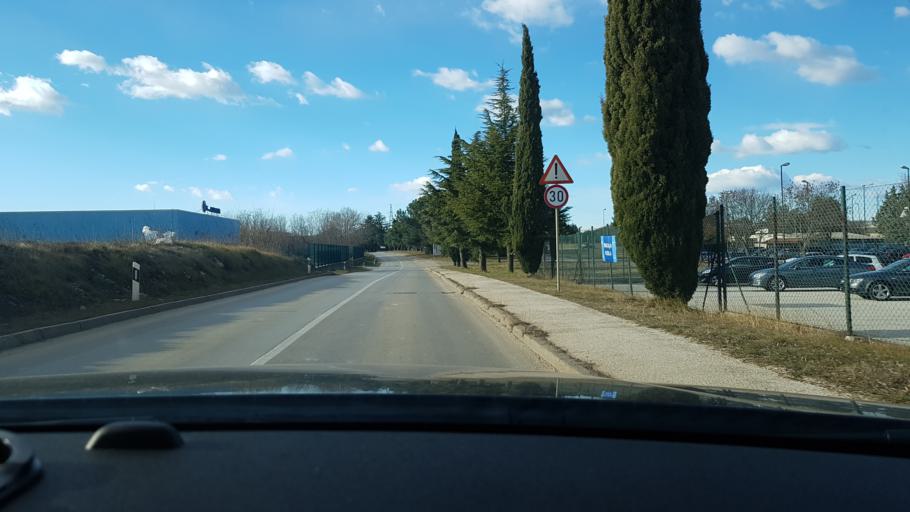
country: HR
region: Istarska
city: Vinez
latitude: 45.1199
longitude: 14.1178
